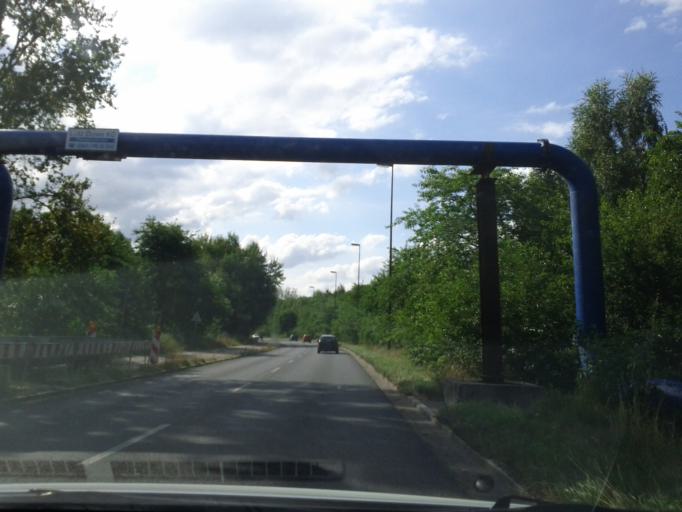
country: DE
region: Bremen
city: Bremen
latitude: 53.1142
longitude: 8.8429
